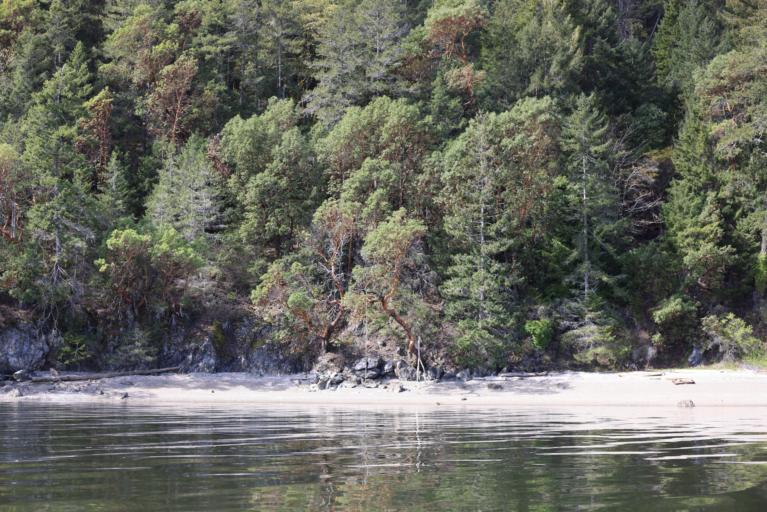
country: CA
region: British Columbia
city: North Saanich
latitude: 48.5933
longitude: -123.5211
